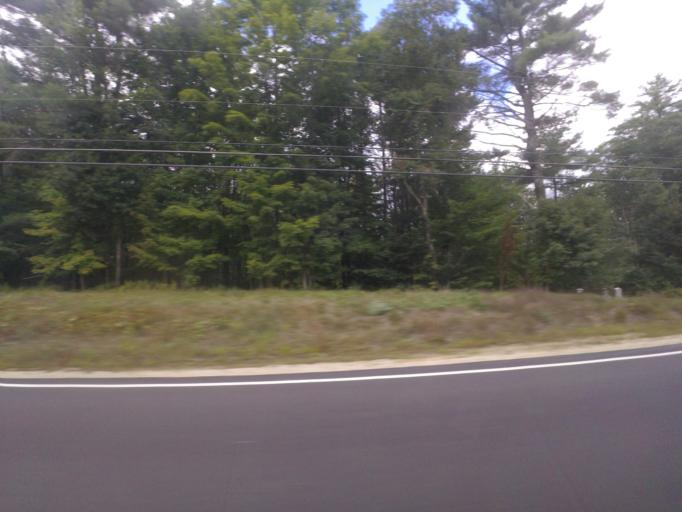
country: US
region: New Hampshire
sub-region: Rockingham County
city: Northwood
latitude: 43.2032
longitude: -71.1030
